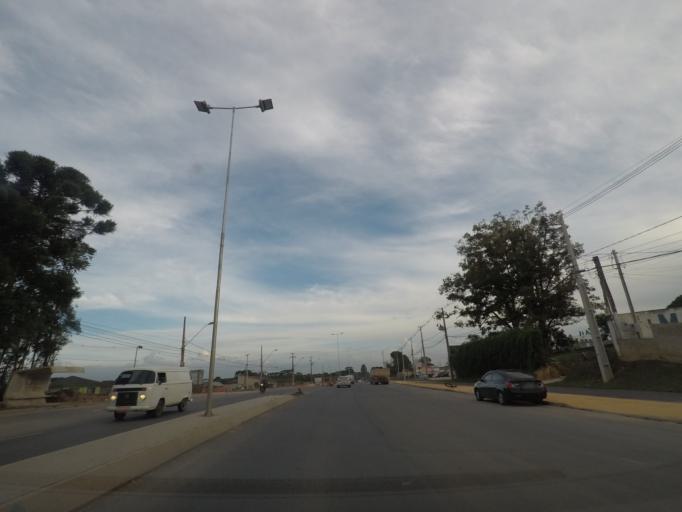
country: BR
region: Parana
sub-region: Colombo
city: Colombo
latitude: -25.3193
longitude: -49.2199
